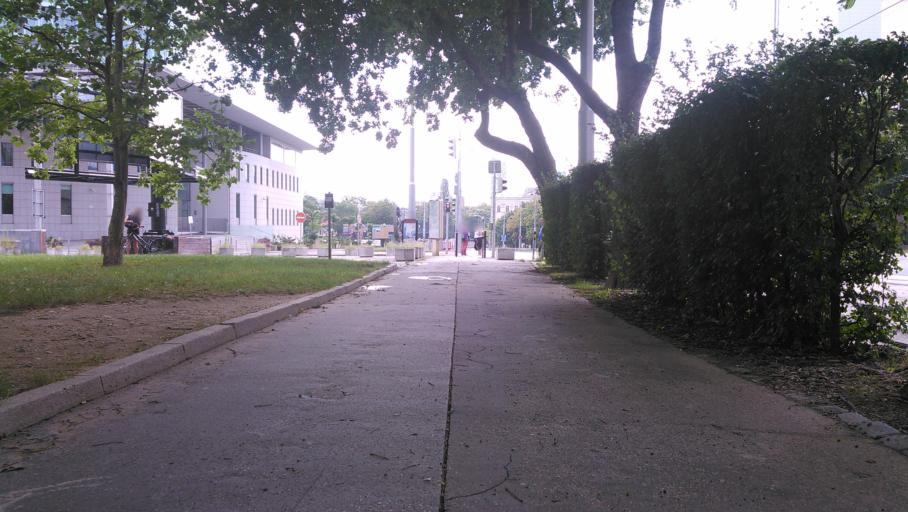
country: SK
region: Bratislavsky
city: Bratislava
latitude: 48.1534
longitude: 17.1135
